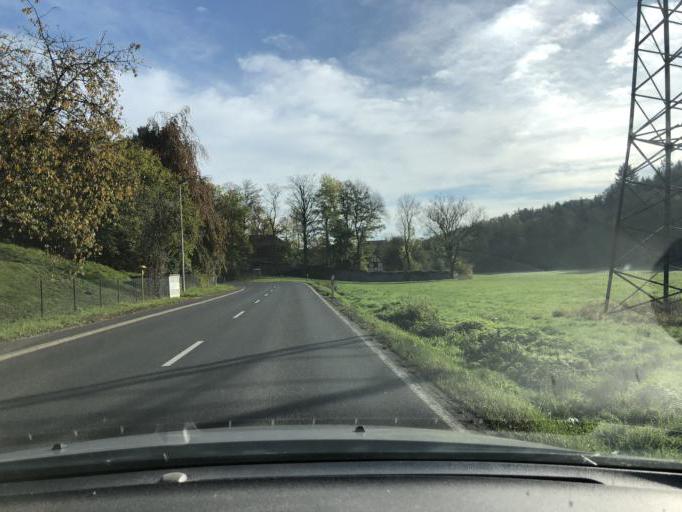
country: DE
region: Thuringia
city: Grimmelshausen
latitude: 50.4914
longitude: 10.6397
